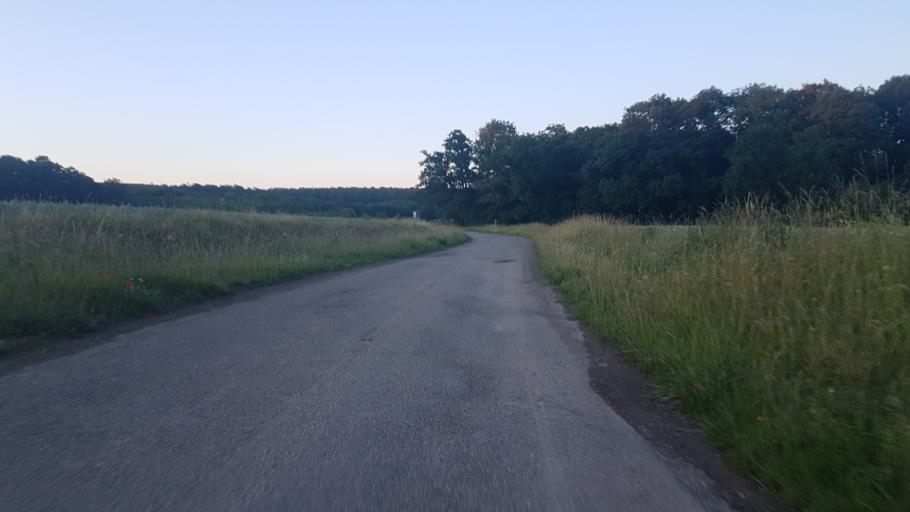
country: DE
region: Baden-Wuerttemberg
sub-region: Regierungsbezirk Stuttgart
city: Guglingen
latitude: 49.1028
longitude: 9.0106
